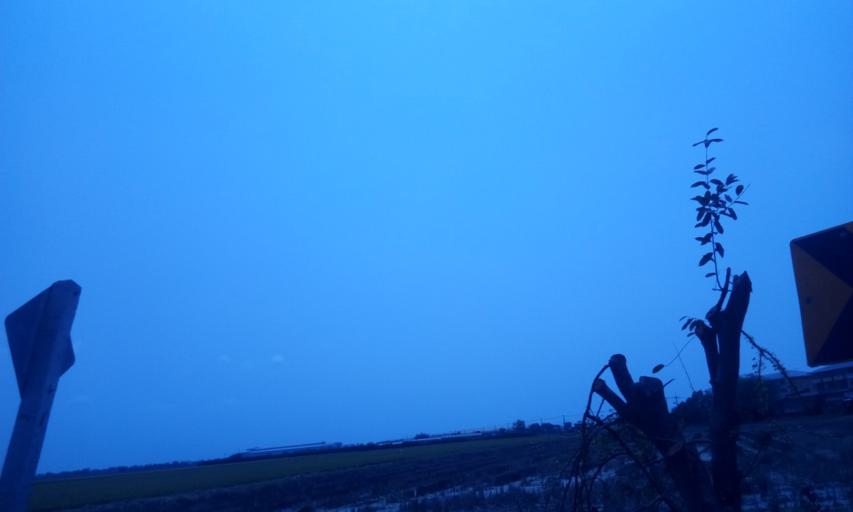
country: TH
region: Chachoengsao
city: Bang Nam Priao
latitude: 13.9669
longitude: 100.9661
